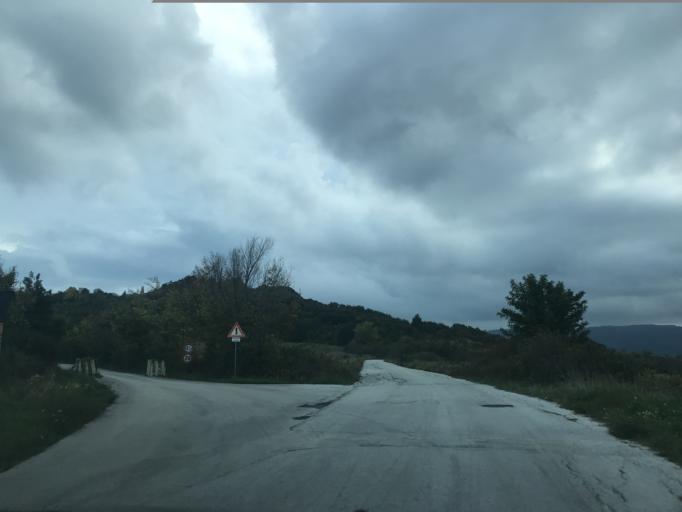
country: IT
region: Molise
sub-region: Provincia di Campobasso
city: Duronia
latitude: 41.6690
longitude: 14.4603
